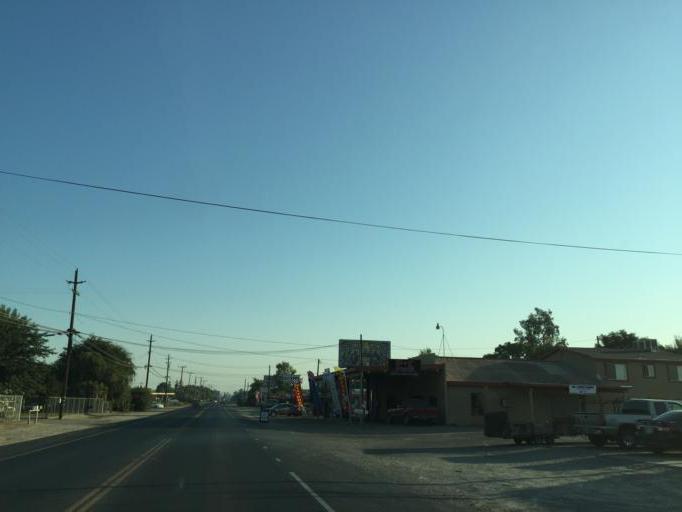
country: US
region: California
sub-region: Tulare County
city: Visalia
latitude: 36.3813
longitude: -119.2968
